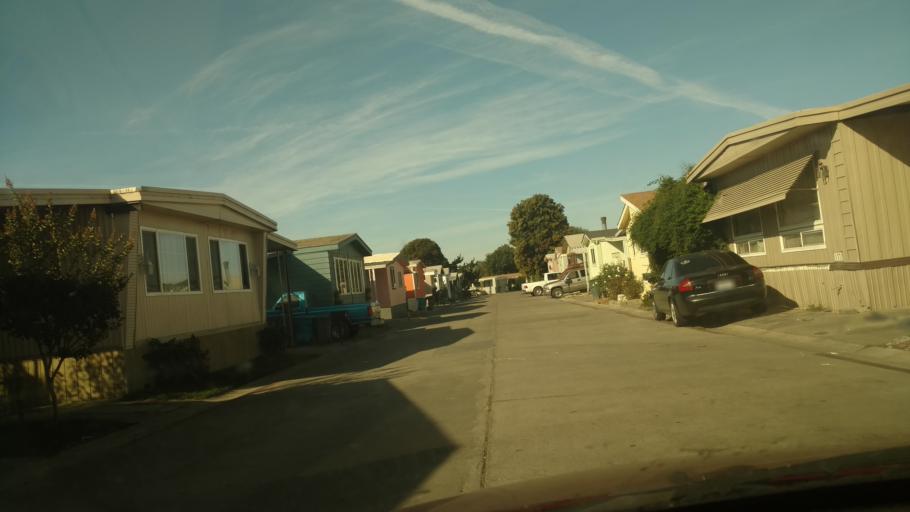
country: US
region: California
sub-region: San Benito County
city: Hollister
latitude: 36.8507
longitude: -121.4208
